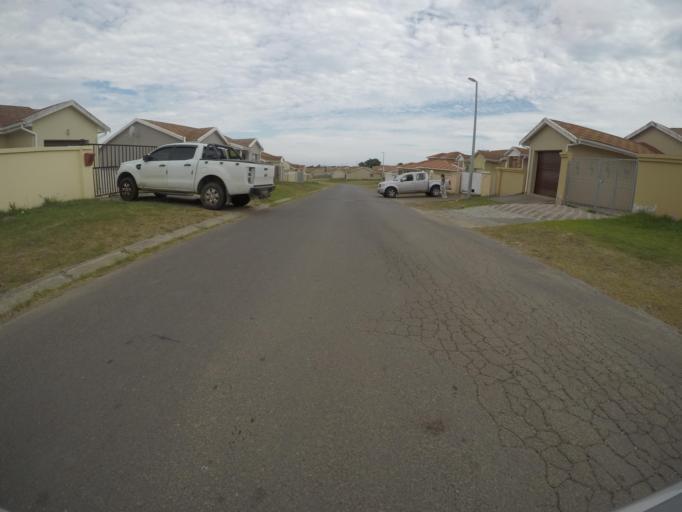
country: ZA
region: Eastern Cape
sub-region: Buffalo City Metropolitan Municipality
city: East London
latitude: -32.9911
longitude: 27.8437
